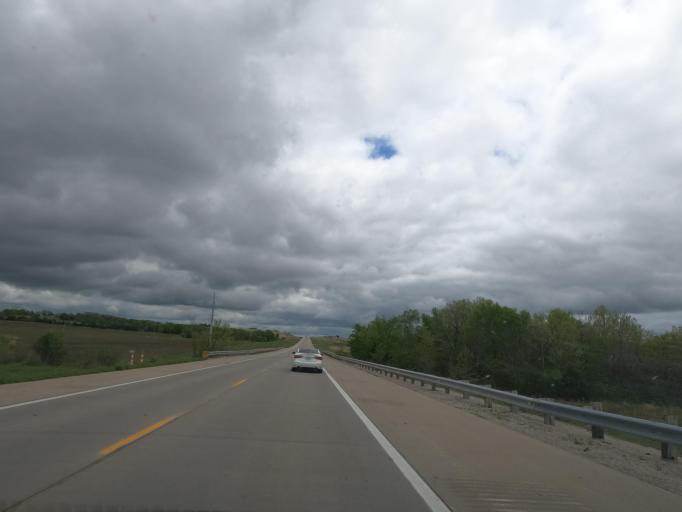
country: US
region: Kansas
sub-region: Montgomery County
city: Cherryvale
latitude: 37.3476
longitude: -95.5797
